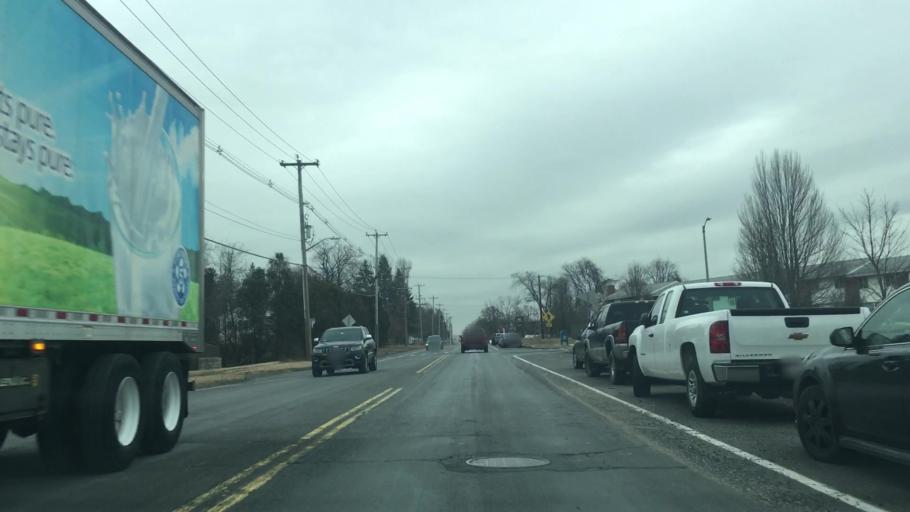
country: US
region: Massachusetts
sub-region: Hampden County
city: Holyoke
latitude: 42.1798
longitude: -72.6400
